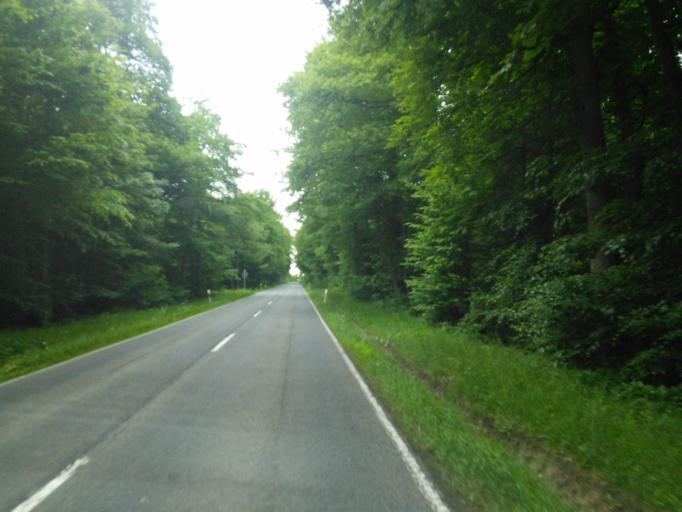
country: DE
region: Rheinland-Pfalz
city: Berg
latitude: 50.5708
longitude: 6.9115
